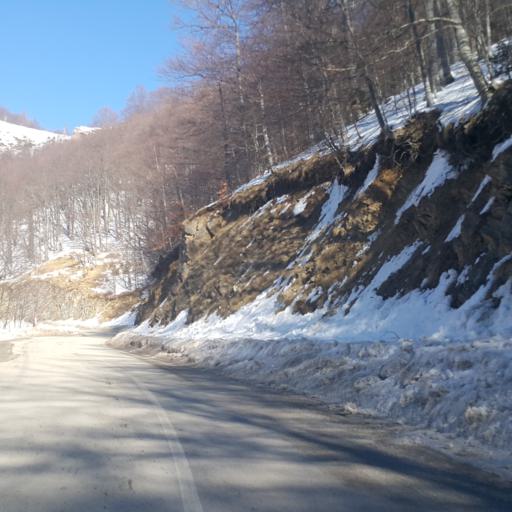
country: XK
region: Mitrovica
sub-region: Komuna e Leposaviqit
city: Leposaviq
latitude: 43.3128
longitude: 20.8604
